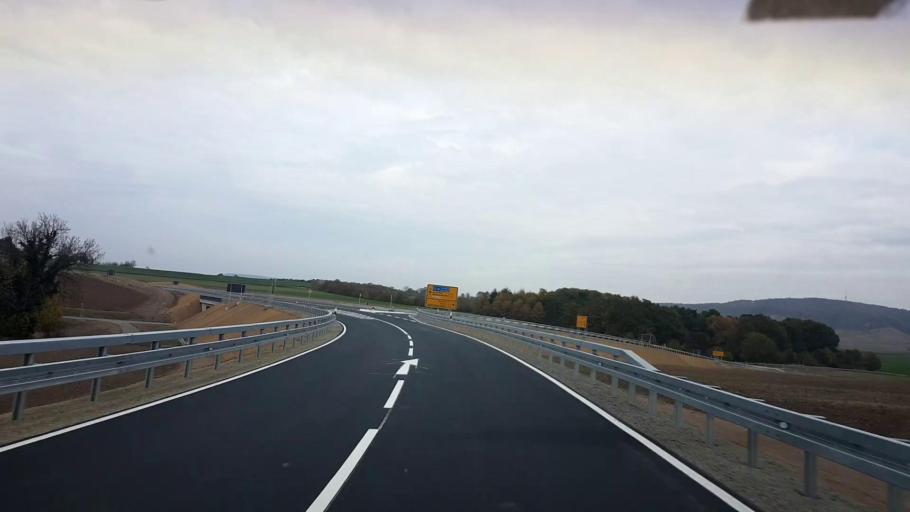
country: DE
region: Bavaria
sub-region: Regierungsbezirk Unterfranken
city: Castell
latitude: 49.7585
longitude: 10.3453
